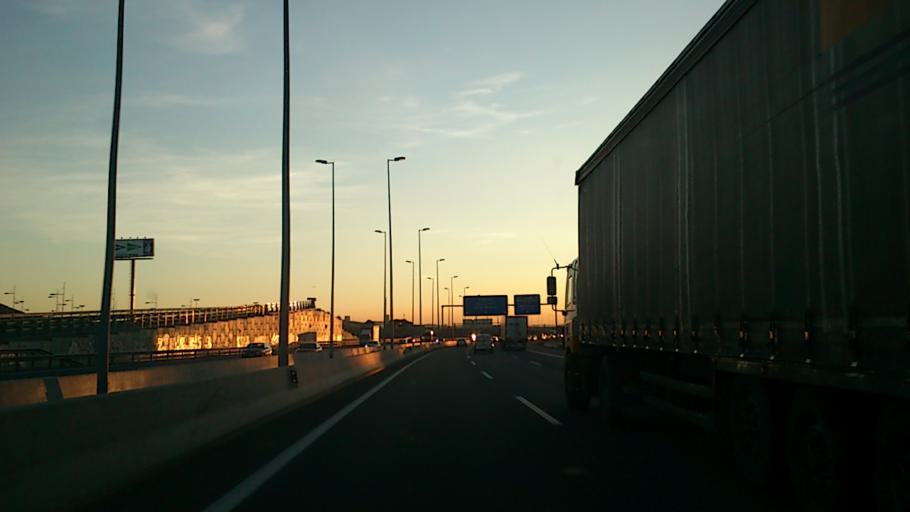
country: ES
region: Madrid
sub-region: Provincia de Madrid
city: Alcala de Henares
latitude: 40.4801
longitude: -3.4034
